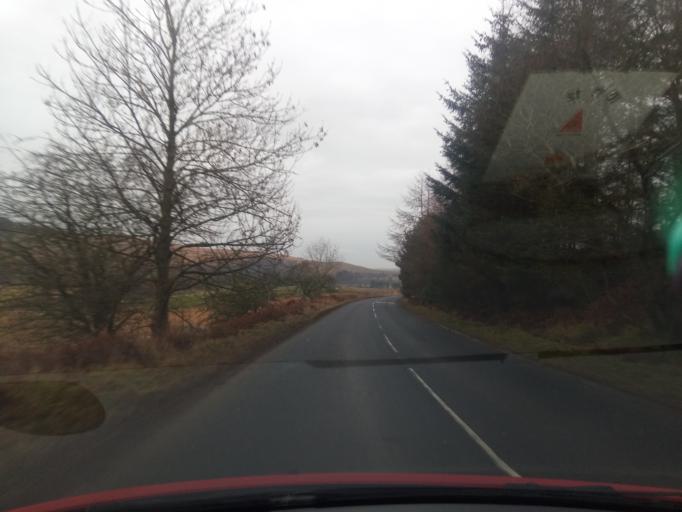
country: GB
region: England
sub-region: Northumberland
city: Haltwhistle
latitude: 55.1777
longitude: -2.4478
